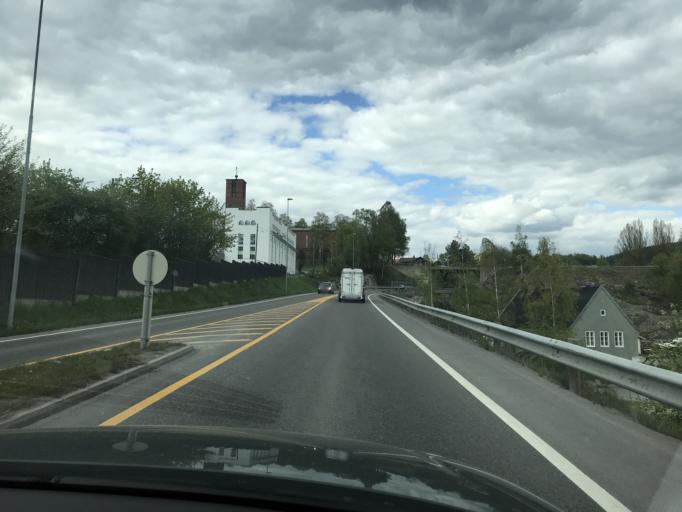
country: NO
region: Telemark
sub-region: Notodden
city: Notodden
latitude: 59.5594
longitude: 9.2657
